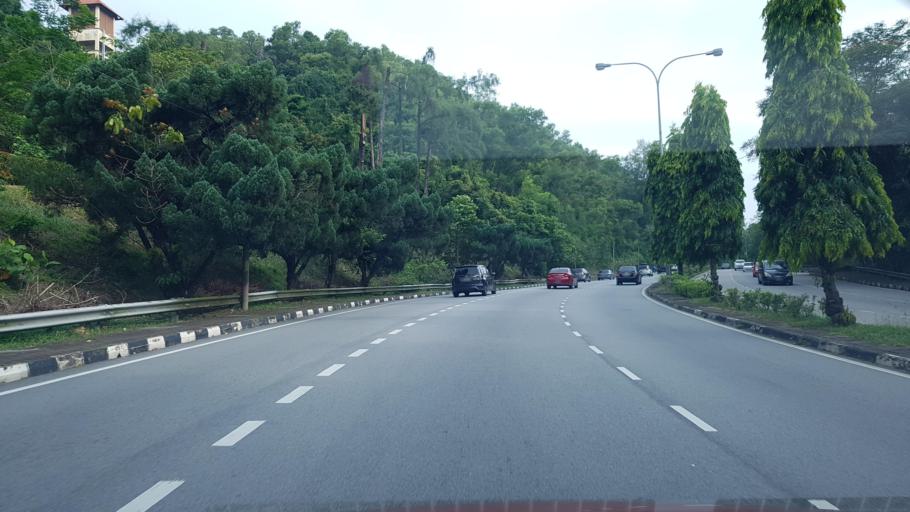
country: MY
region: Terengganu
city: Kuala Terengganu
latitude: 5.3229
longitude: 103.1366
